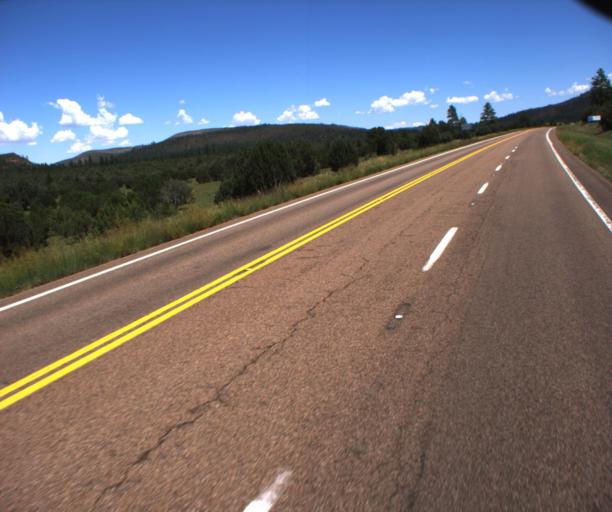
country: US
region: Arizona
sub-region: Navajo County
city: Linden
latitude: 34.0536
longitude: -110.2175
